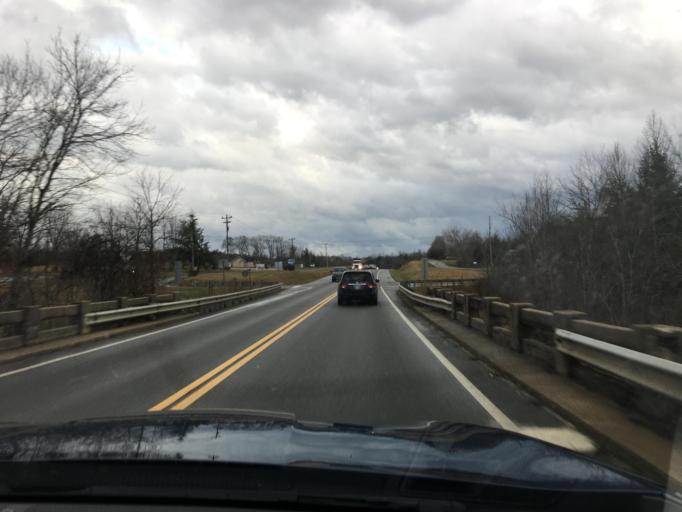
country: US
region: Tennessee
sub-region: Cumberland County
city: Crossville
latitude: 35.9170
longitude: -84.9956
